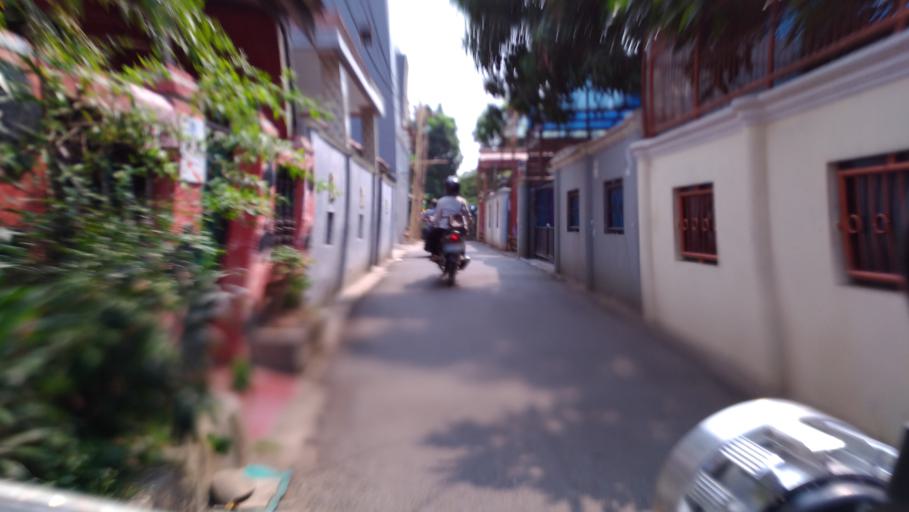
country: ID
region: West Java
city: Cileungsir
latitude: -6.3523
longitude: 106.8935
